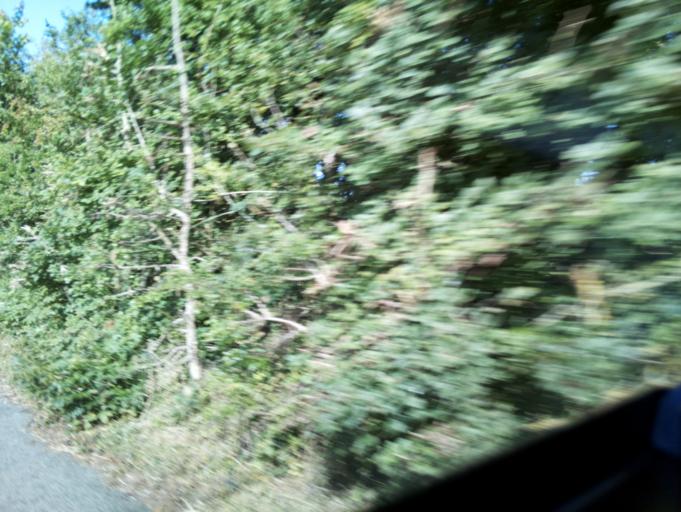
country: GB
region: England
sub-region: Oxfordshire
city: Bampton
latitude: 51.7067
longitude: -1.5056
